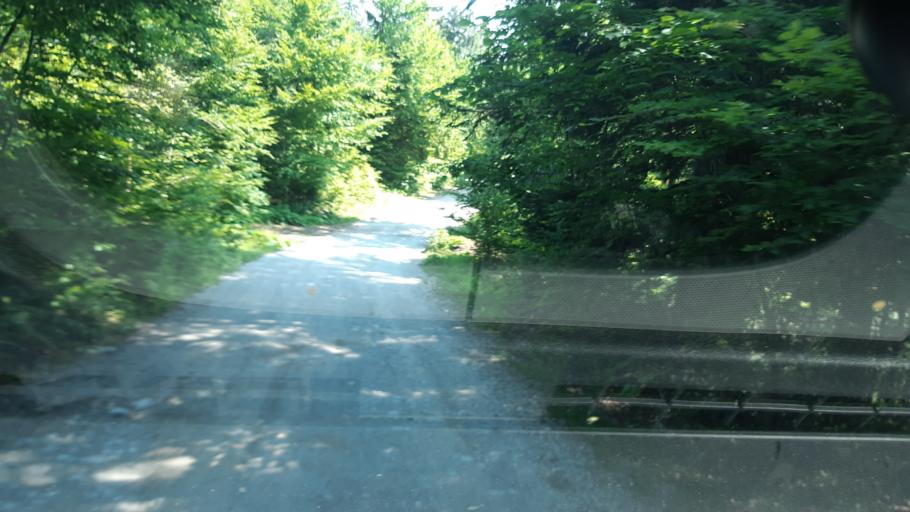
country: SI
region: Trzic
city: Bistrica pri Trzicu
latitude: 46.3761
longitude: 14.2763
